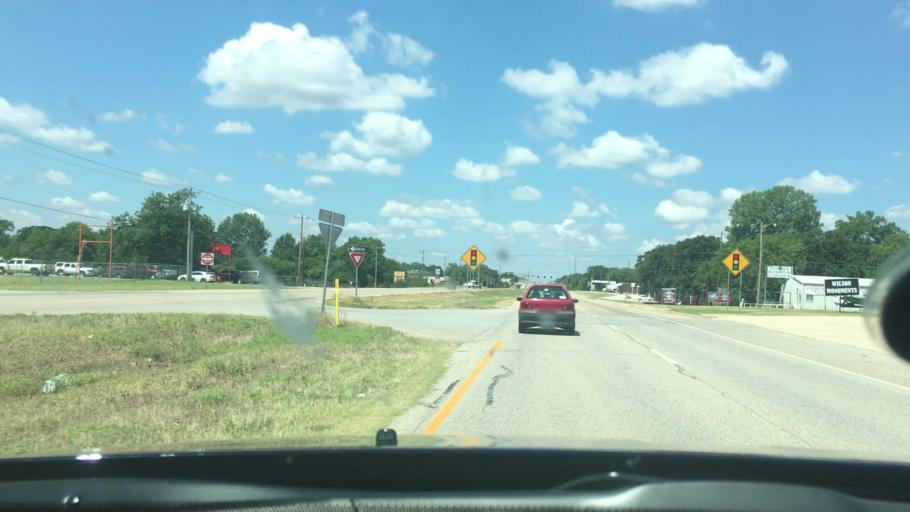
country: US
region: Oklahoma
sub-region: Carter County
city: Lone Grove
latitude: 34.1729
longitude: -97.2258
